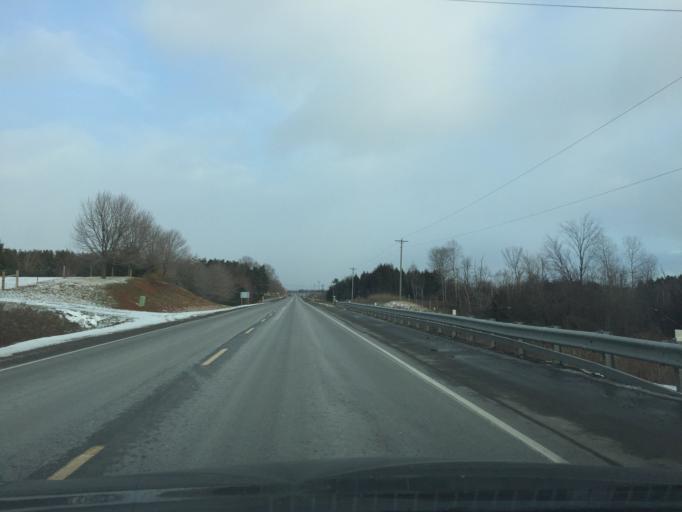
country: CA
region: Ontario
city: Uxbridge
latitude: 44.0659
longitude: -79.0372
